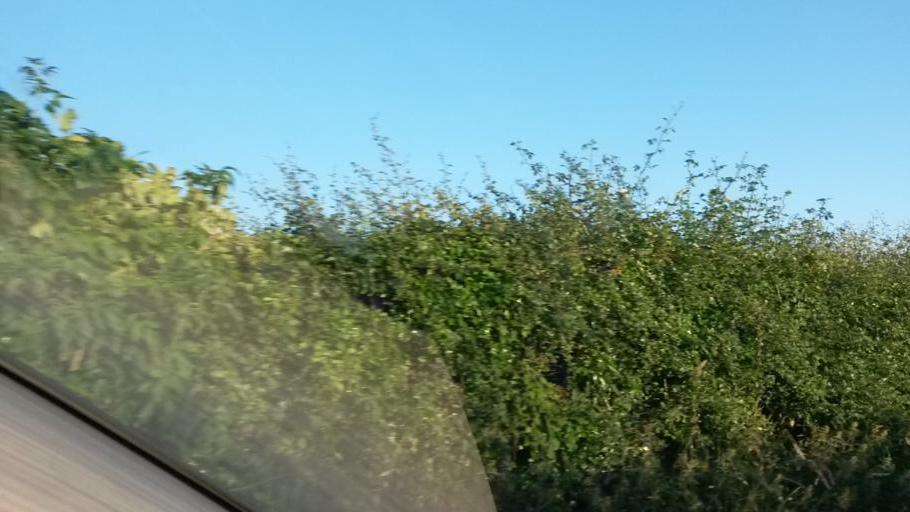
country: IE
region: Leinster
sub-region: An Mhi
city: Ashbourne
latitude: 53.5425
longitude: -6.3620
